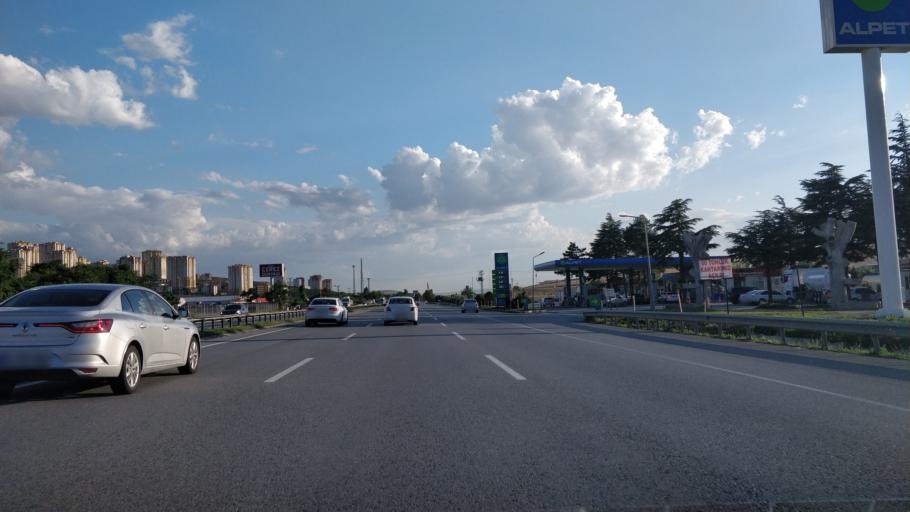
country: TR
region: Ankara
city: Etimesgut
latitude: 39.8272
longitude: 32.5765
